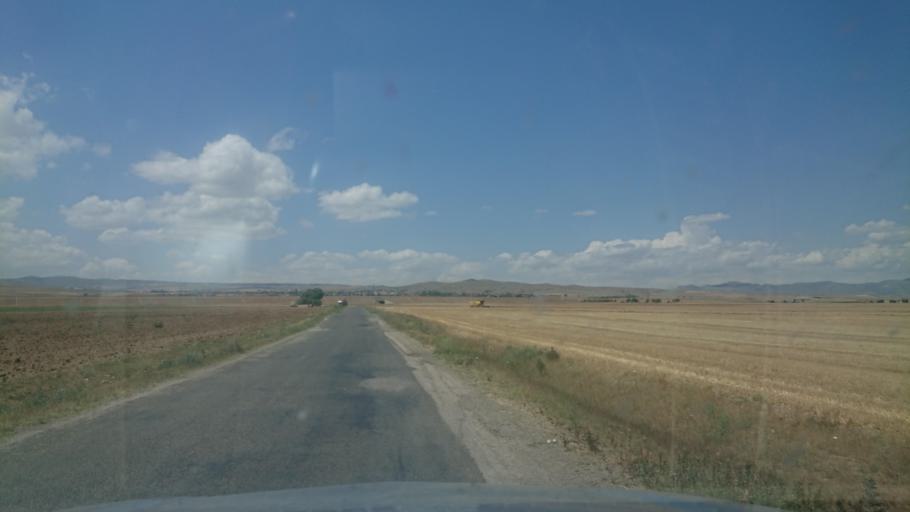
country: TR
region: Aksaray
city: Sariyahsi
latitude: 38.9956
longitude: 33.8773
